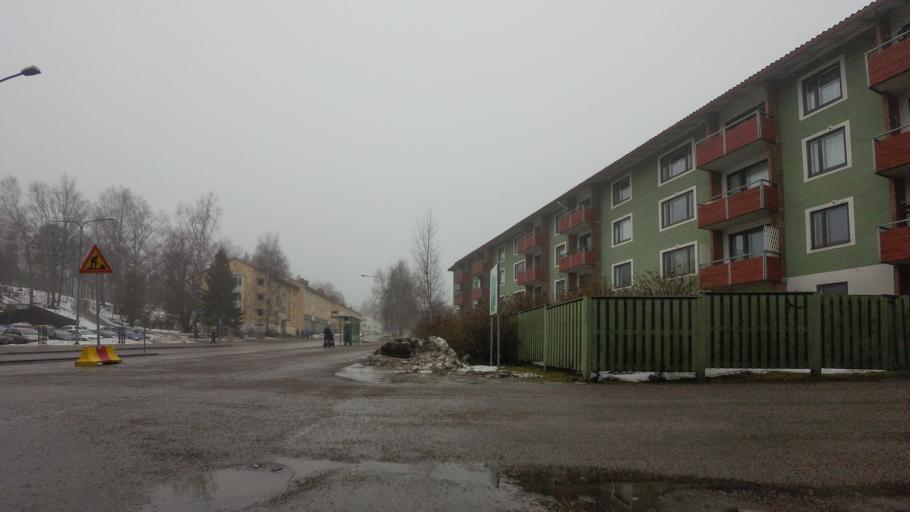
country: FI
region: Uusimaa
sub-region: Helsinki
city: Vantaa
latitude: 60.2064
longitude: 25.0453
